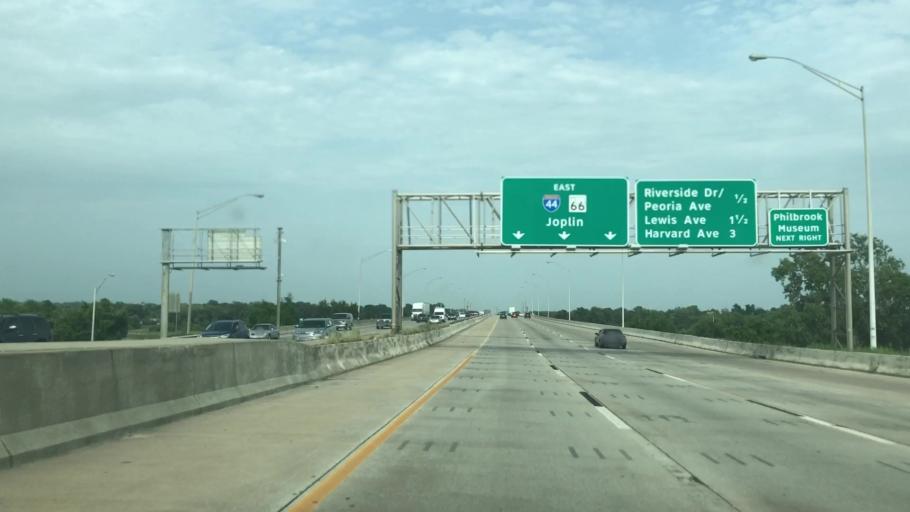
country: US
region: Oklahoma
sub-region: Tulsa County
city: Tulsa
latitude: 36.0898
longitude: -95.9934
